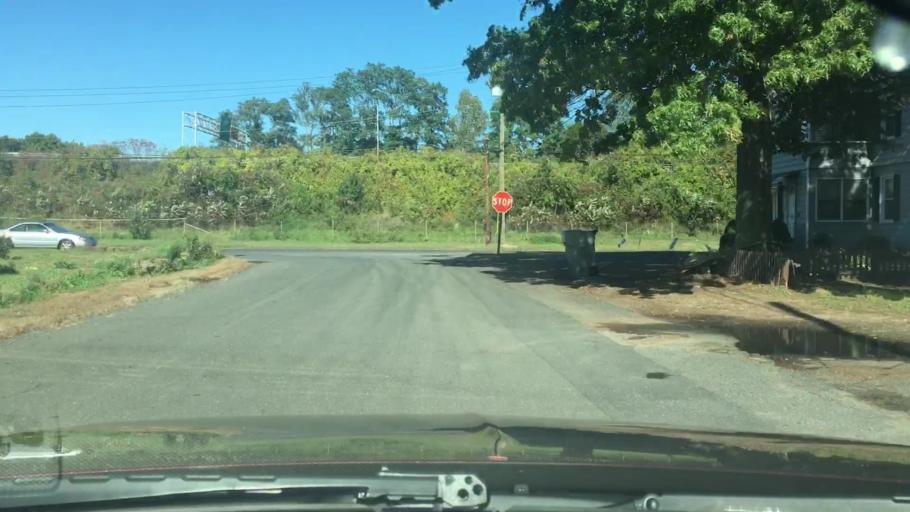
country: US
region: Connecticut
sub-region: Hartford County
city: Plainville
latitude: 41.6744
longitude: -72.8537
